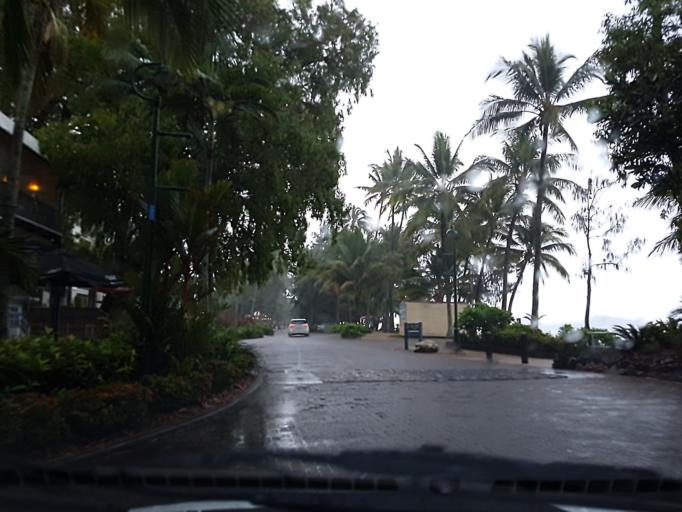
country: AU
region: Queensland
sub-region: Cairns
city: Palm Cove
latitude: -16.7471
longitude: 145.6709
